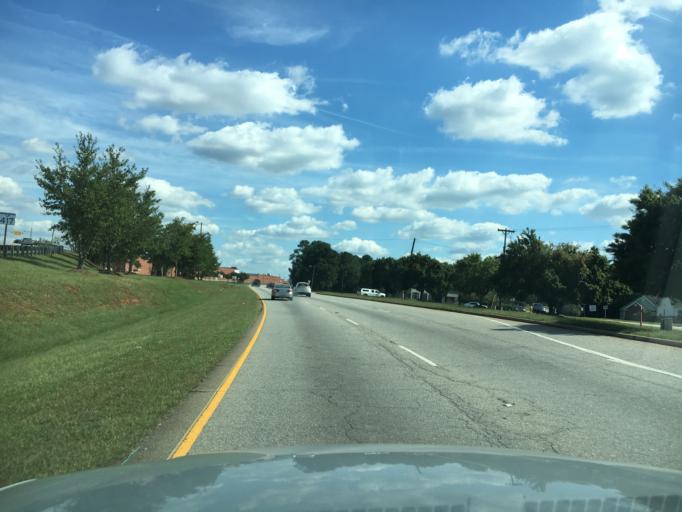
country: US
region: South Carolina
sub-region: Greenville County
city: Mauldin
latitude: 34.7741
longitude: -82.3050
